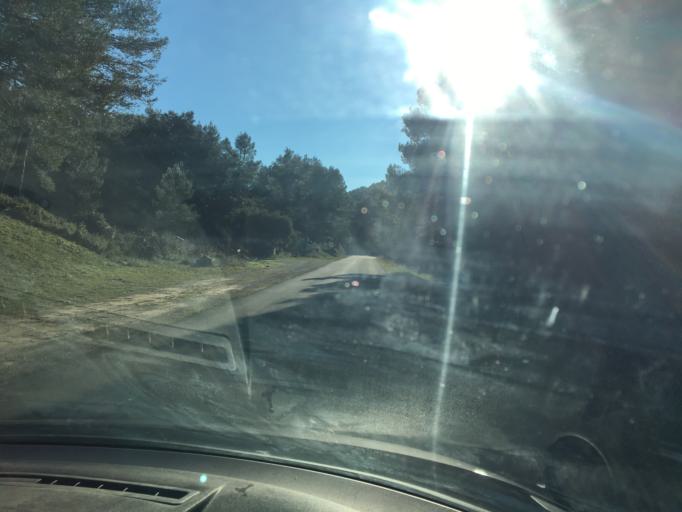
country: FR
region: Provence-Alpes-Cote d'Azur
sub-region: Departement des Bouches-du-Rhone
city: Saint-Remy-de-Provence
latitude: 43.7713
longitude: 4.7940
